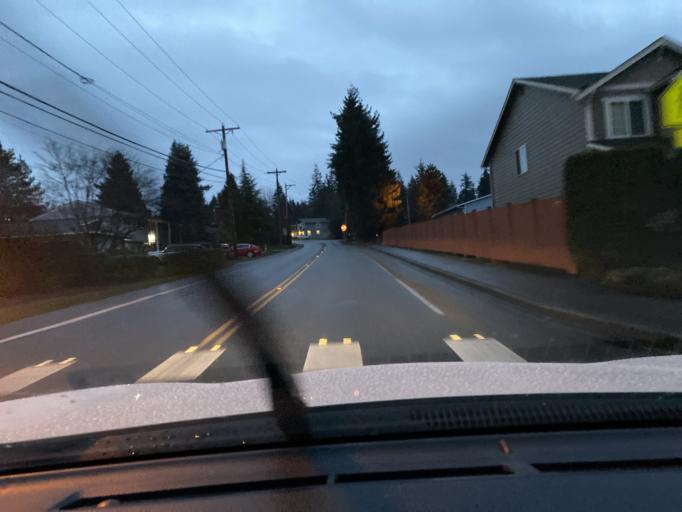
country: US
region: Washington
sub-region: Snohomish County
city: Martha Lake
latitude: 47.8707
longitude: -122.2604
